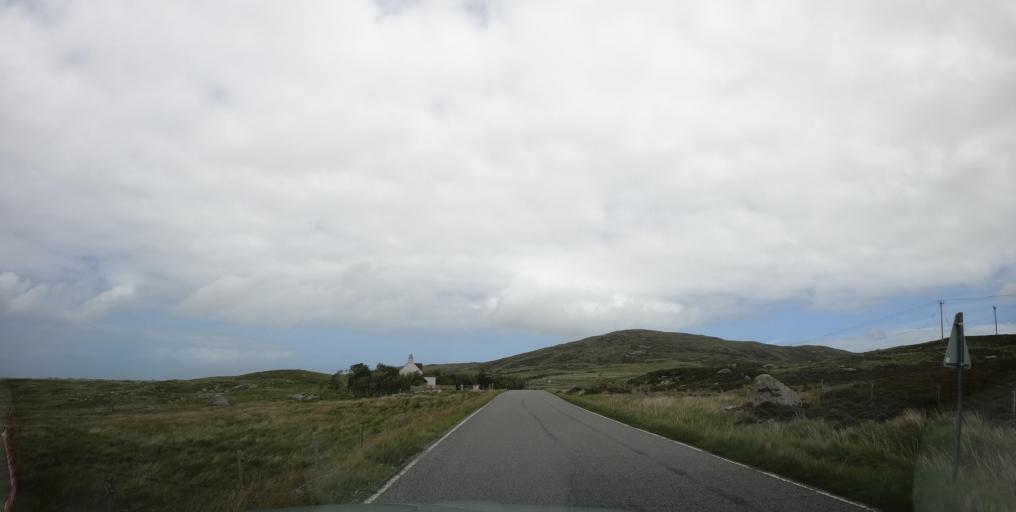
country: GB
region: Scotland
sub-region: Eilean Siar
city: Isle of South Uist
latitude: 57.2928
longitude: -7.3653
